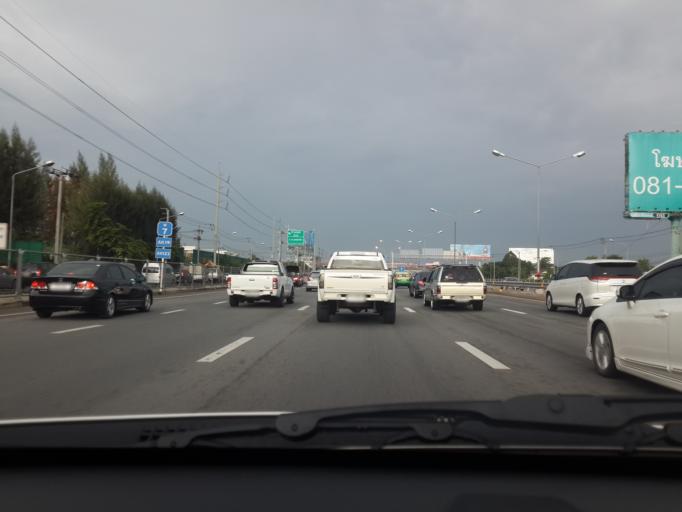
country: TH
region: Bangkok
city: Suan Luang
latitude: 13.7399
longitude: 100.6497
